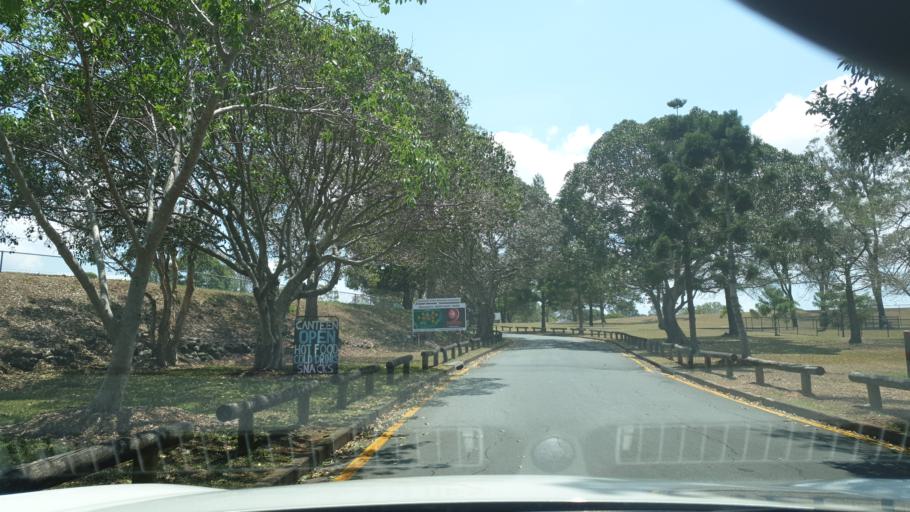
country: AU
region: Queensland
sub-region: Brisbane
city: Chermside West
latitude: -27.3777
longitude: 153.0295
